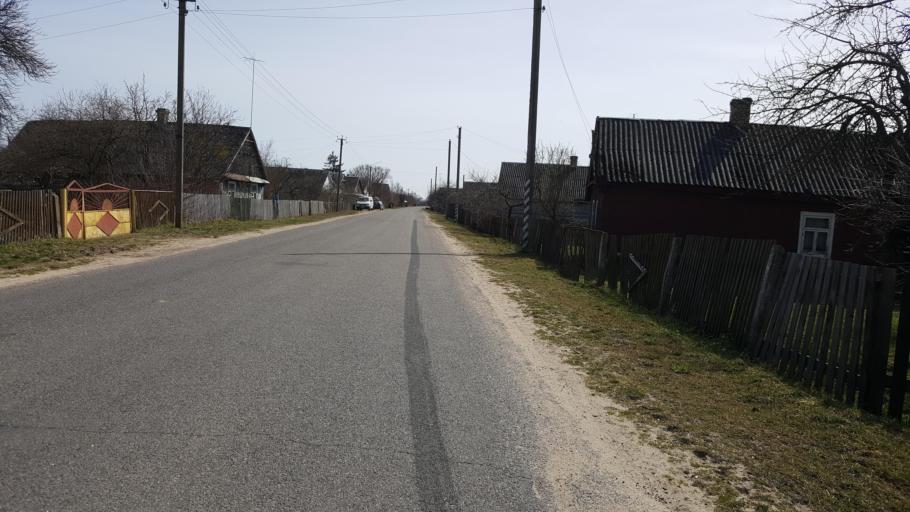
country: BY
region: Brest
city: Kamyanyuki
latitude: 52.4893
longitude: 23.8727
